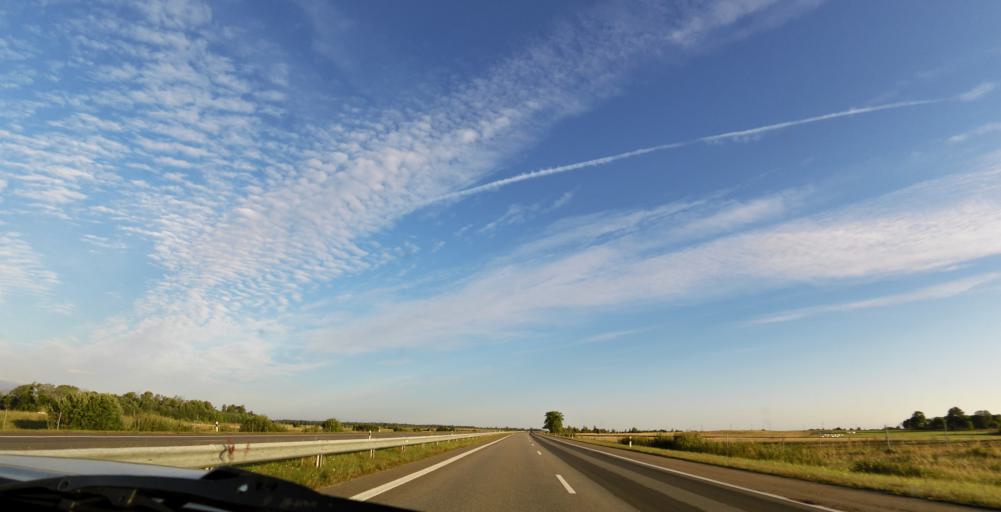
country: LT
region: Vilnius County
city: Ukmerge
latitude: 55.1501
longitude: 24.8245
